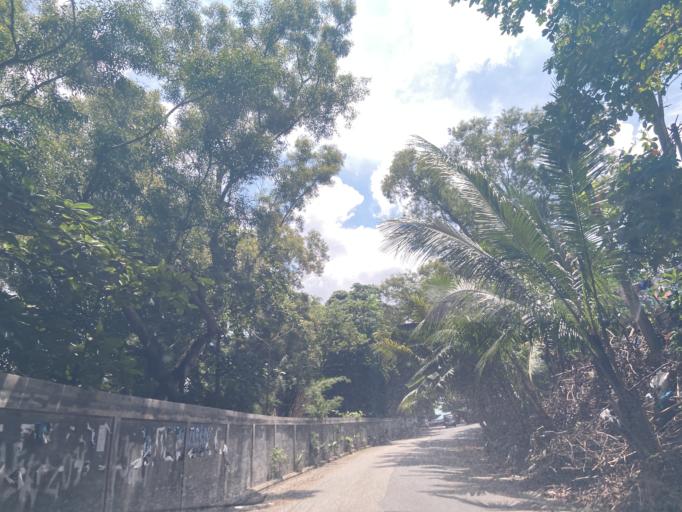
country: SG
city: Singapore
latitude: 1.1549
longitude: 104.0137
